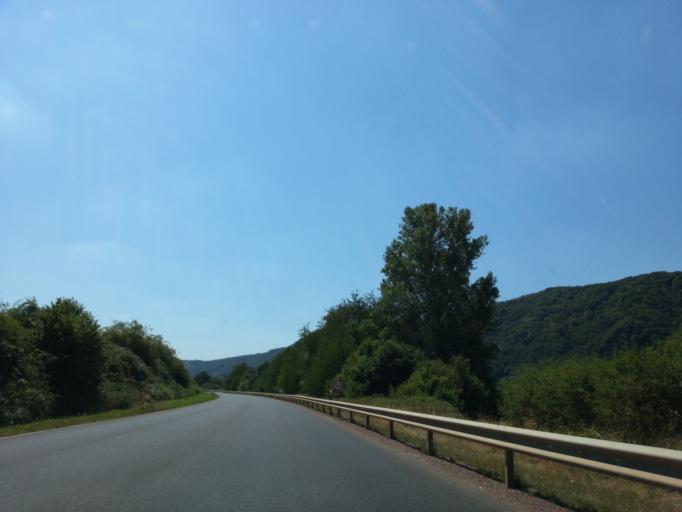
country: DE
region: Rheinland-Pfalz
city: Piesport
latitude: 49.8751
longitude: 6.9016
